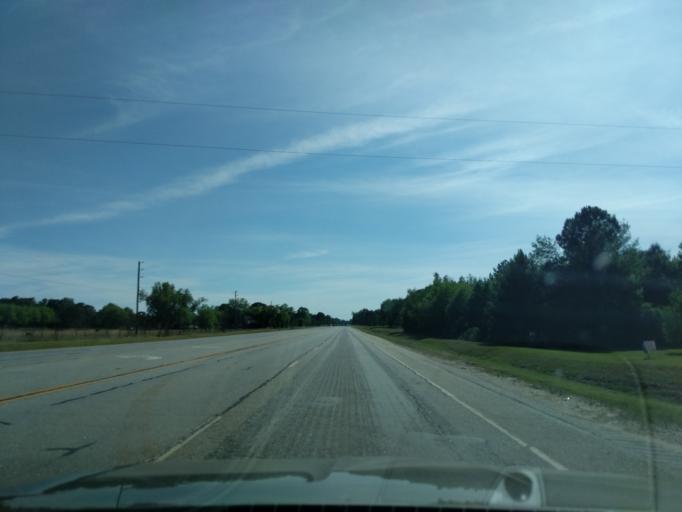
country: US
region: Georgia
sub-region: Jefferson County
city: Wrens
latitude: 33.2275
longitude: -82.3620
